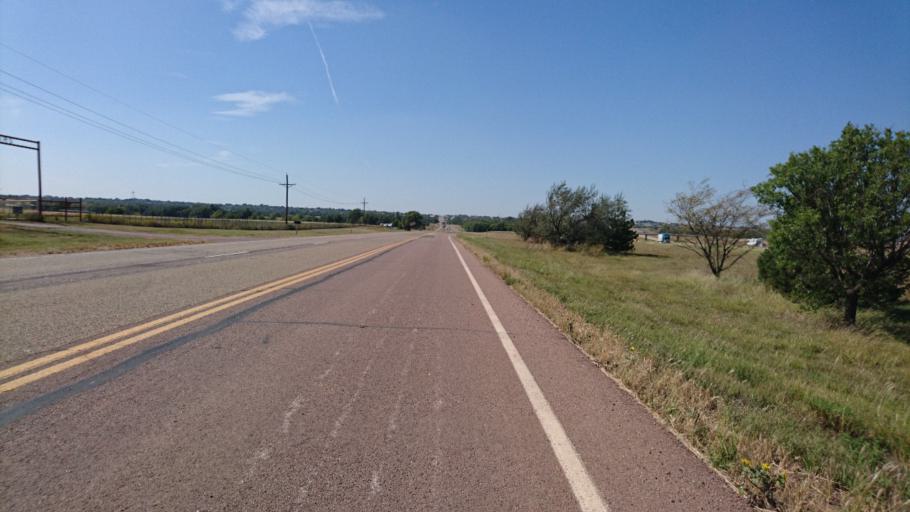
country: US
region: Texas
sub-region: Wheeler County
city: Shamrock
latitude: 35.2266
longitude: -100.2207
